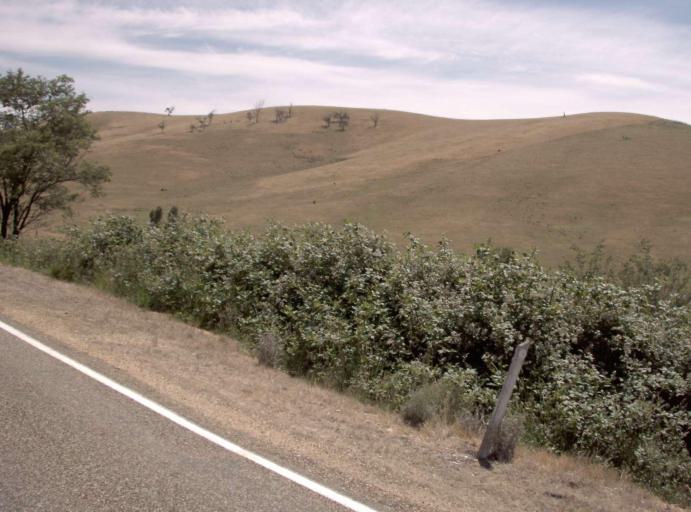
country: AU
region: Victoria
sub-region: Alpine
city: Mount Beauty
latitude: -37.0577
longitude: 147.6183
